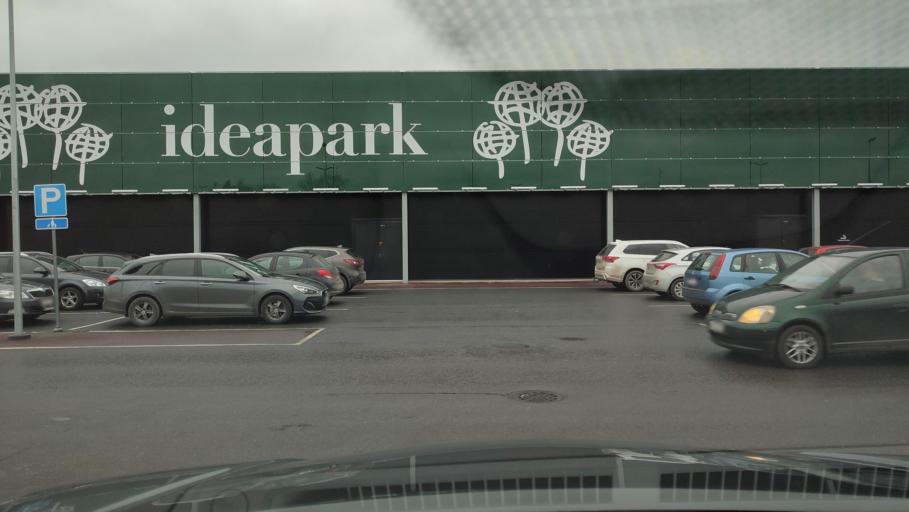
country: FI
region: Southern Ostrobothnia
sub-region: Seinaejoki
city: Seinaejoki
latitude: 62.7930
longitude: 22.7909
